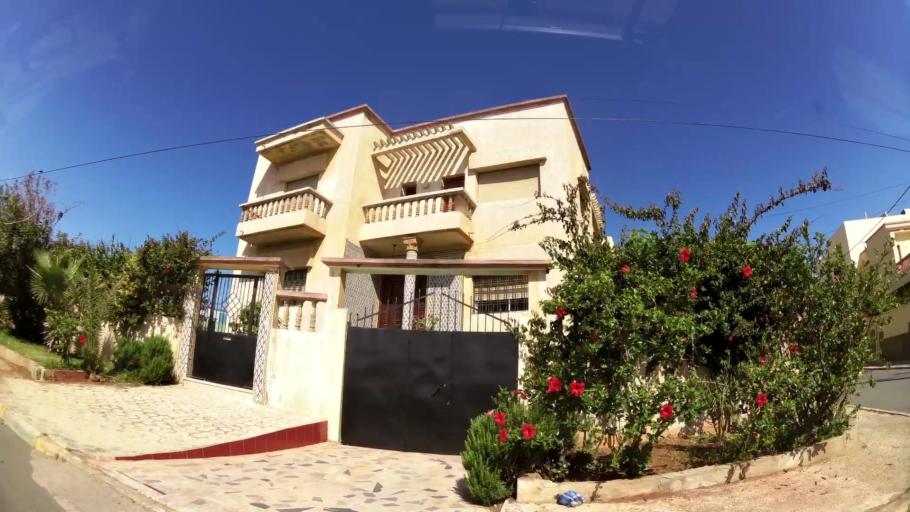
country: MA
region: Rabat-Sale-Zemmour-Zaer
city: Sale
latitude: 34.0678
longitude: -6.8035
